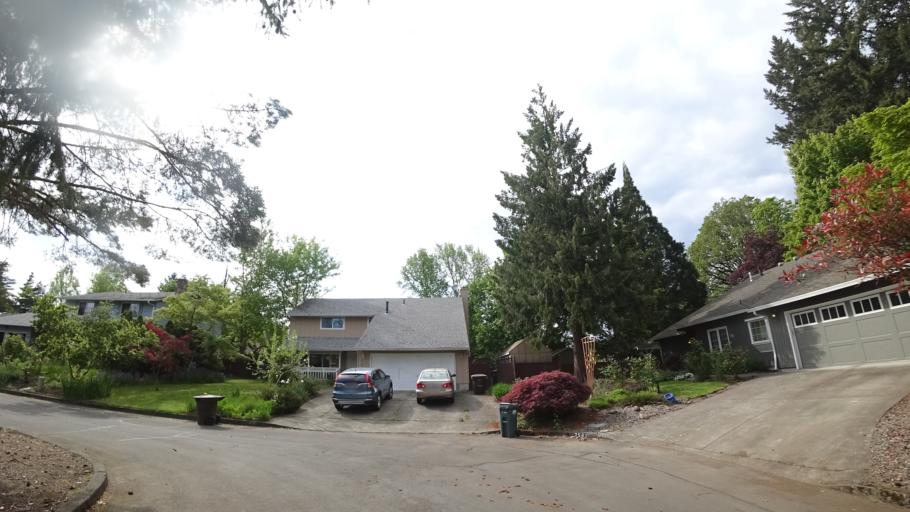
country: US
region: Oregon
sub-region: Washington County
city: Hillsboro
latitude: 45.4979
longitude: -122.9566
